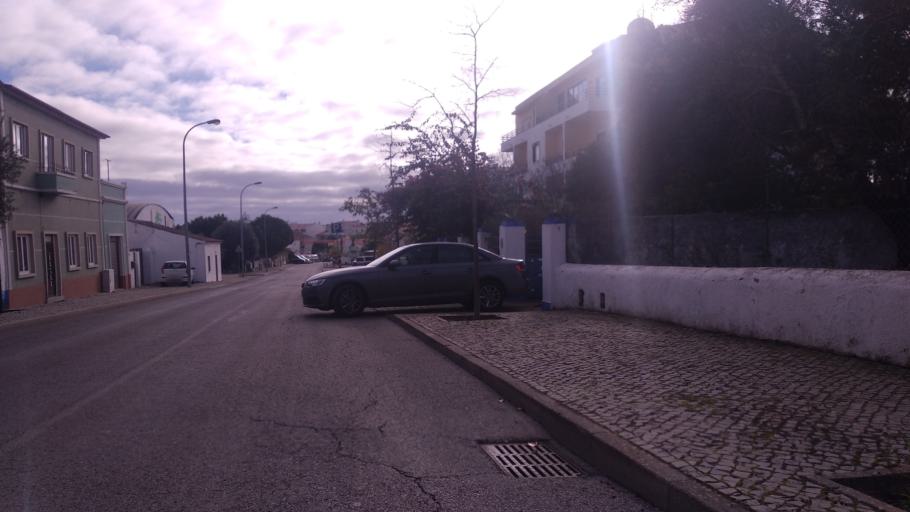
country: PT
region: Faro
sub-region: Sao Bras de Alportel
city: Sao Bras de Alportel
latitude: 37.1578
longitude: -7.8940
